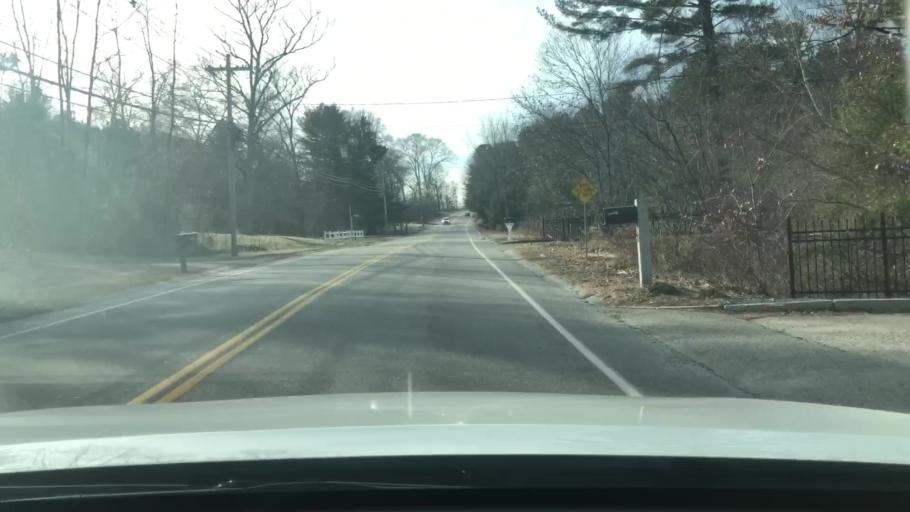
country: US
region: Massachusetts
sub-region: Worcester County
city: Grafton
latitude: 42.2015
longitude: -71.7046
